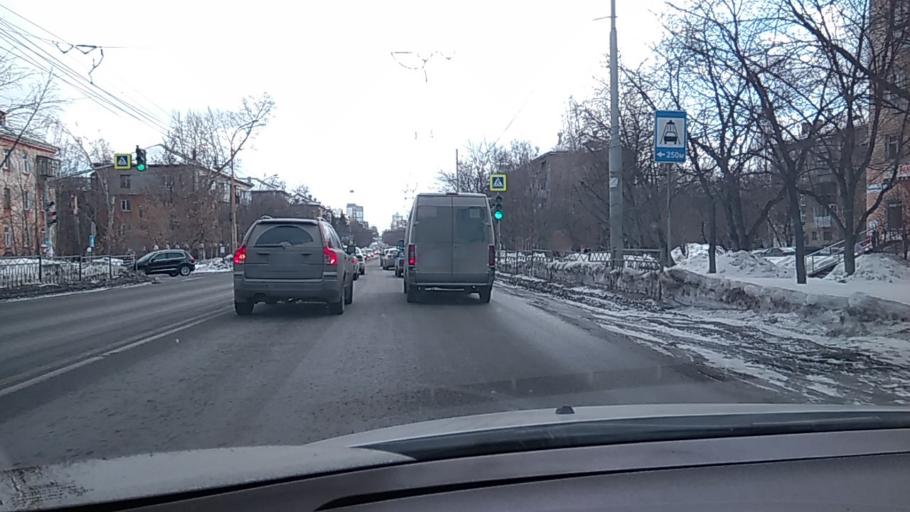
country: RU
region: Sverdlovsk
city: Yekaterinburg
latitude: 56.8533
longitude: 60.6551
